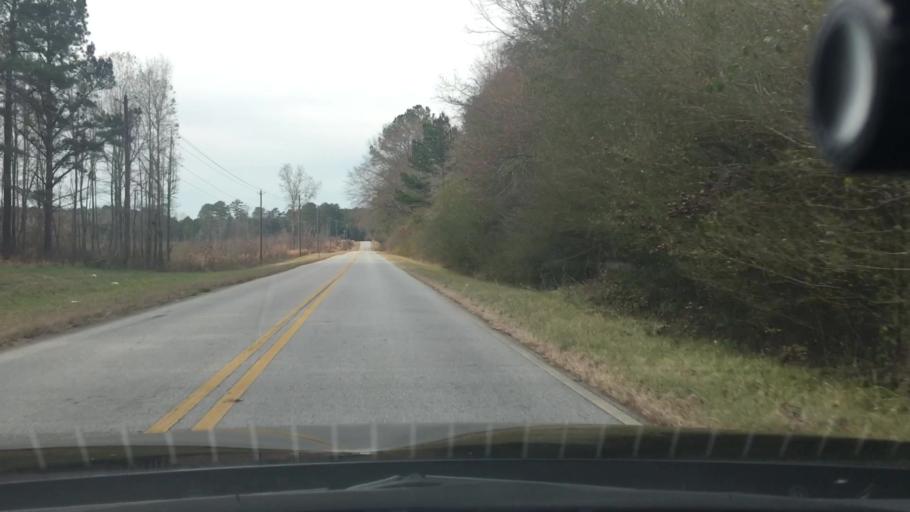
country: US
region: Georgia
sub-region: Spalding County
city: Experiment
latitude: 33.2737
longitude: -84.3593
